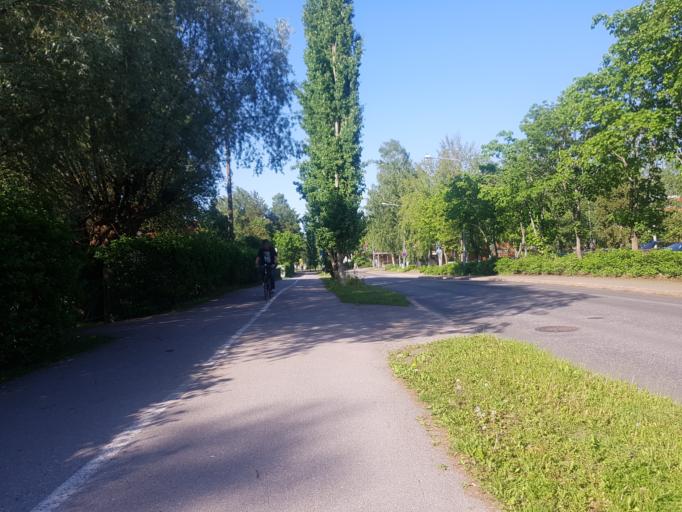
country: FI
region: Uusimaa
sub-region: Helsinki
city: Vantaa
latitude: 60.2545
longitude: 24.9946
